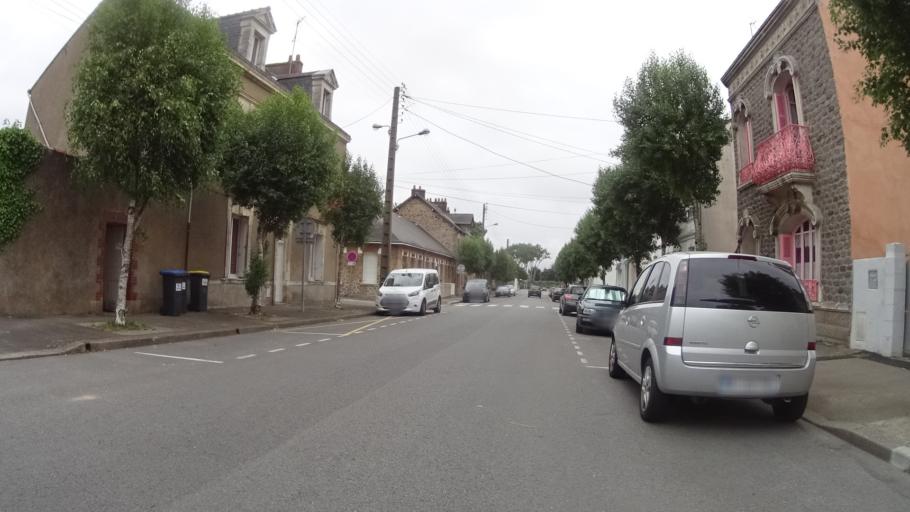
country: FR
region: Pays de la Loire
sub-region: Departement de la Loire-Atlantique
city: Trignac
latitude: 47.2986
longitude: -2.1872
